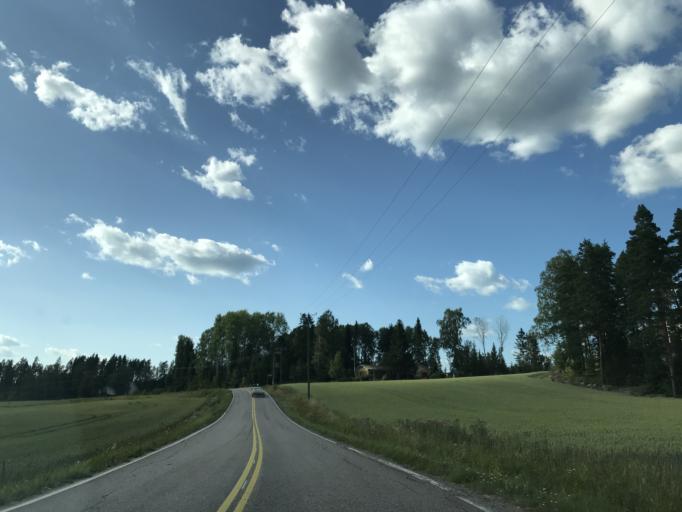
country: FI
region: Uusimaa
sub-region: Helsinki
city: Nurmijaervi
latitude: 60.4487
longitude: 24.6550
